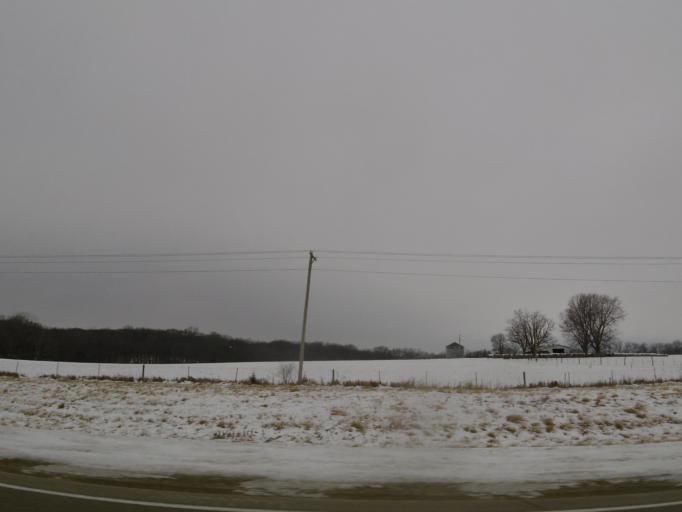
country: US
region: Illinois
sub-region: Hancock County
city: Nauvoo
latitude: 40.5684
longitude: -91.5655
